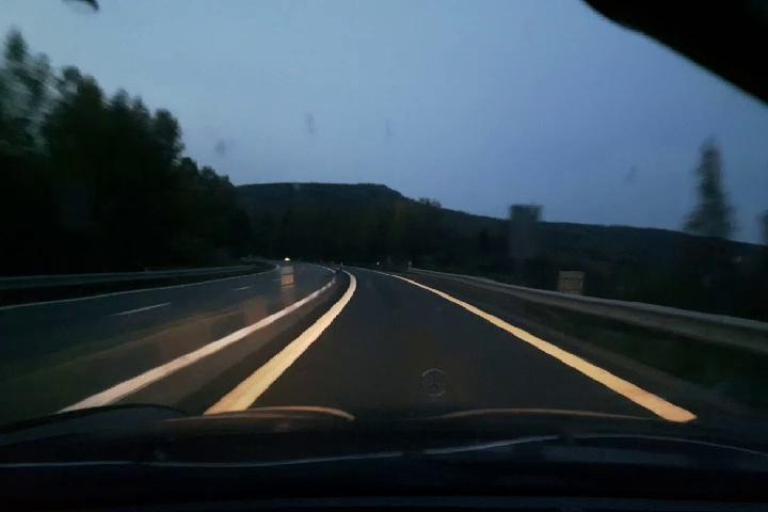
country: SE
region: Vaesternorrland
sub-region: Kramfors Kommun
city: Nordingra
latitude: 63.0640
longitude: 18.3561
